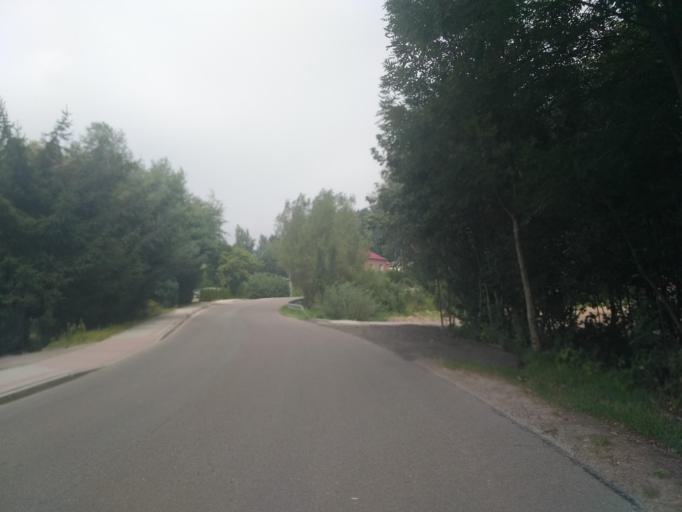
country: PL
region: Subcarpathian Voivodeship
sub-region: Powiat rzeszowski
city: Chmielnik
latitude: 49.9948
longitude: 22.1036
